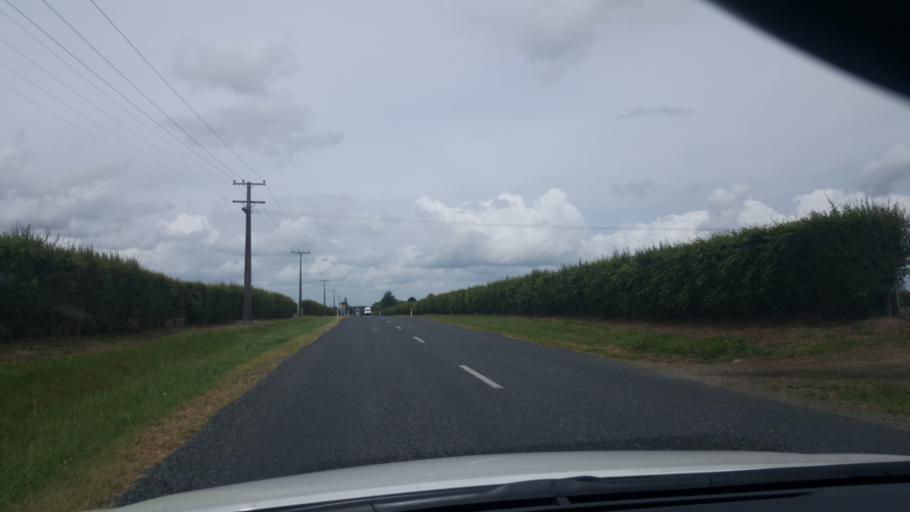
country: NZ
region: Waikato
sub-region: Matamata-Piako District
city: Matamata
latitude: -37.8789
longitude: 175.7290
